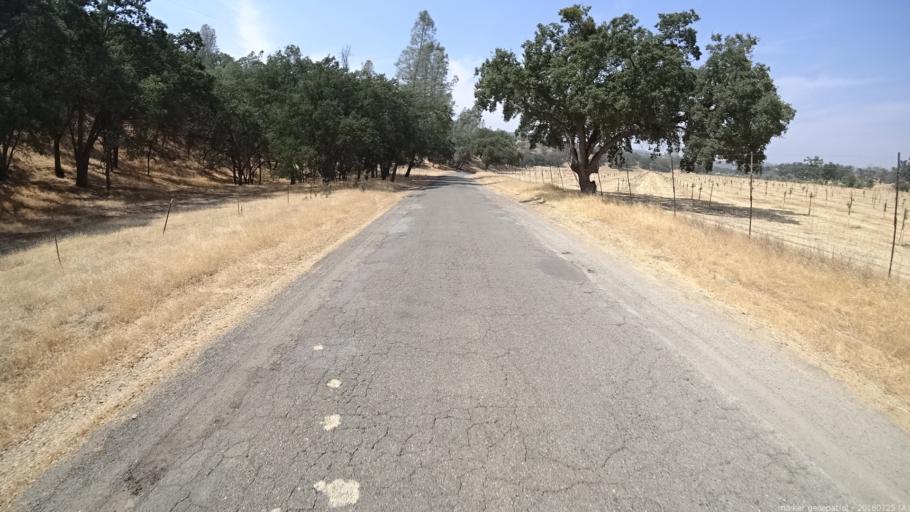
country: US
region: California
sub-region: Fresno County
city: Coalinga
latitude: 35.9213
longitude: -120.4444
